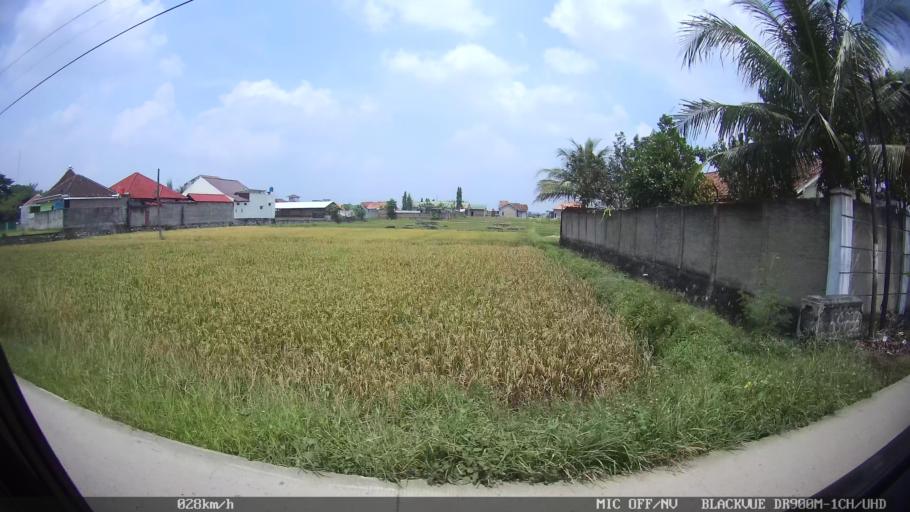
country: ID
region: Lampung
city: Pringsewu
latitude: -5.3513
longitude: 104.9905
